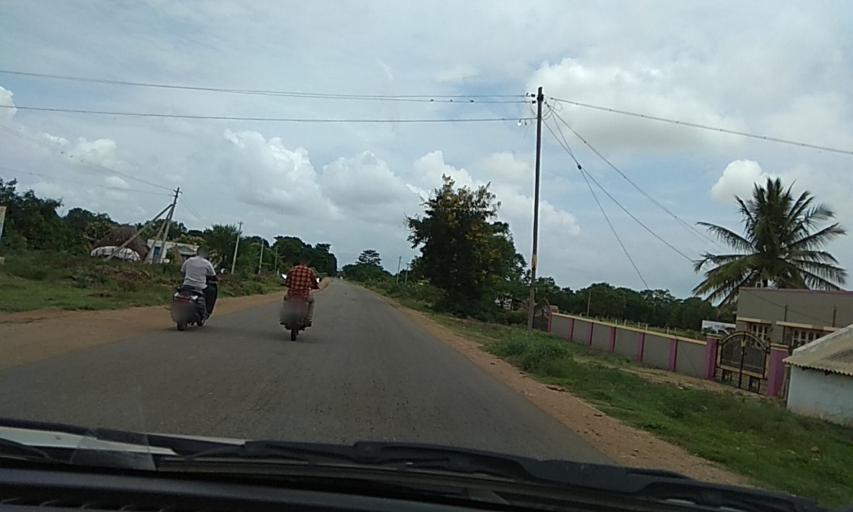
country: IN
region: Karnataka
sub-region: Chamrajnagar
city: Gundlupet
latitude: 11.8109
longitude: 76.7368
